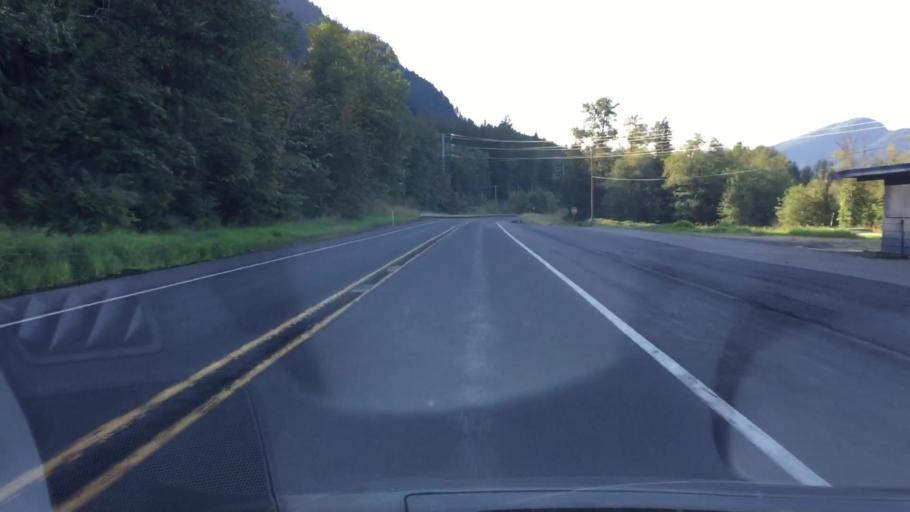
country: US
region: Washington
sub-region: Lewis County
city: Morton
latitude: 46.5321
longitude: -122.2437
